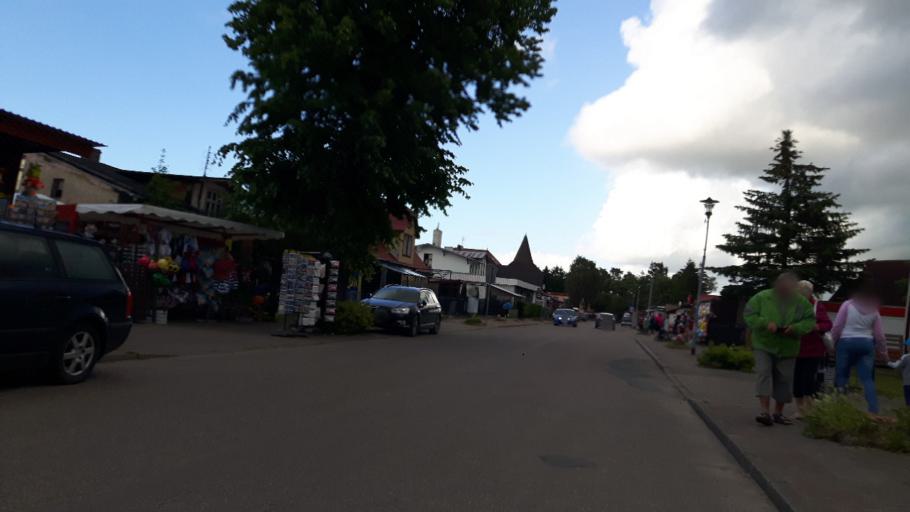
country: PL
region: West Pomeranian Voivodeship
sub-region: Powiat kolobrzeski
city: Ustronie Morskie
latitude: 54.2083
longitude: 15.7254
